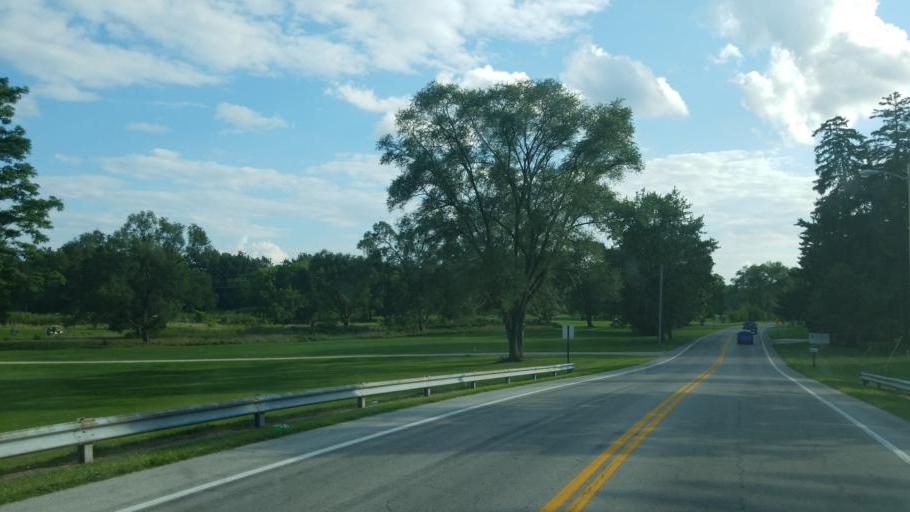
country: US
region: Ohio
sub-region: Sandusky County
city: Ballville
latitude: 41.3328
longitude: -83.1221
